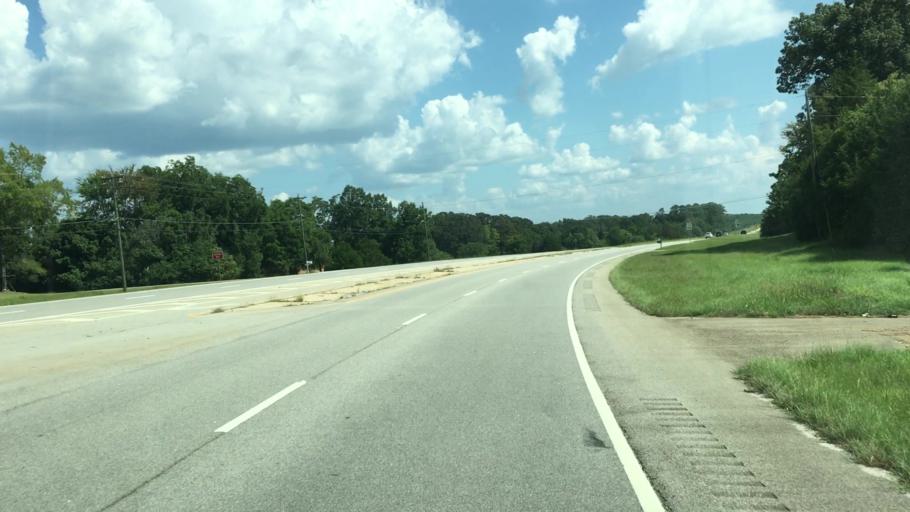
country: US
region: Georgia
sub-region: Putnam County
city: Eatonton
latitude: 33.2680
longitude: -83.3365
